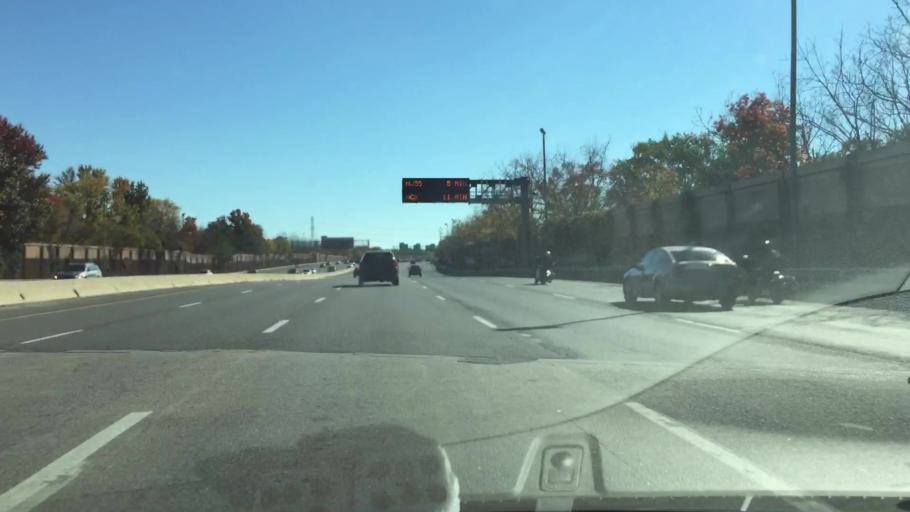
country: US
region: New Jersey
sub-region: Camden County
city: Gloucester City
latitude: 39.8952
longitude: -75.1077
